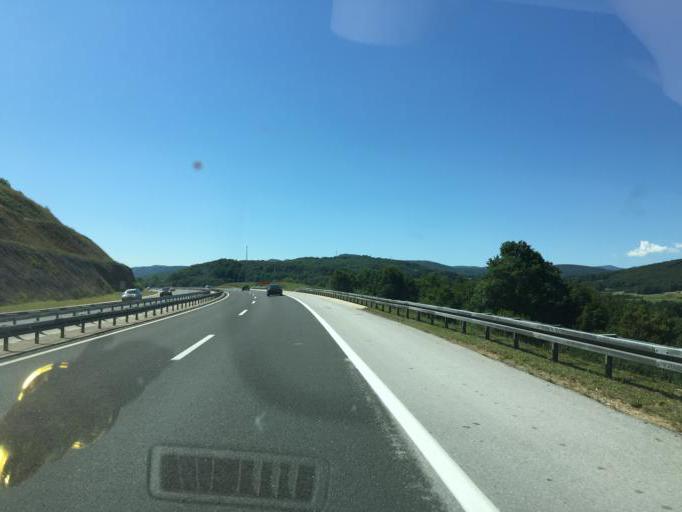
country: HR
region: Licko-Senjska
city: Otocac
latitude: 44.8986
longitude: 15.1842
